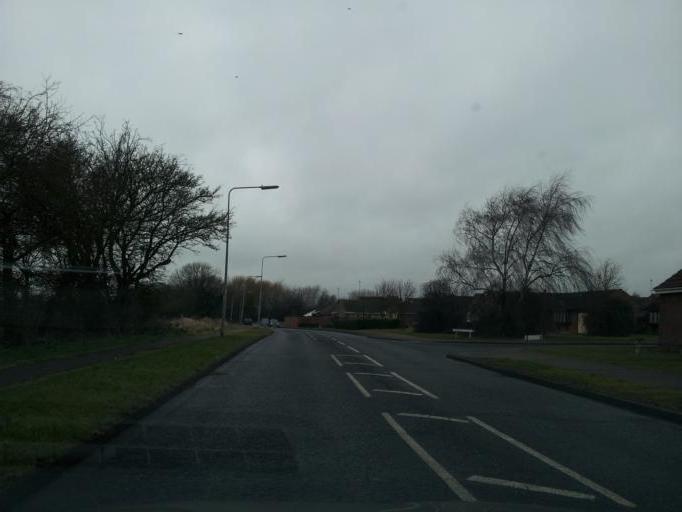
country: GB
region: England
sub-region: Essex
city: Dovercourt
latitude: 51.9246
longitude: 1.2523
